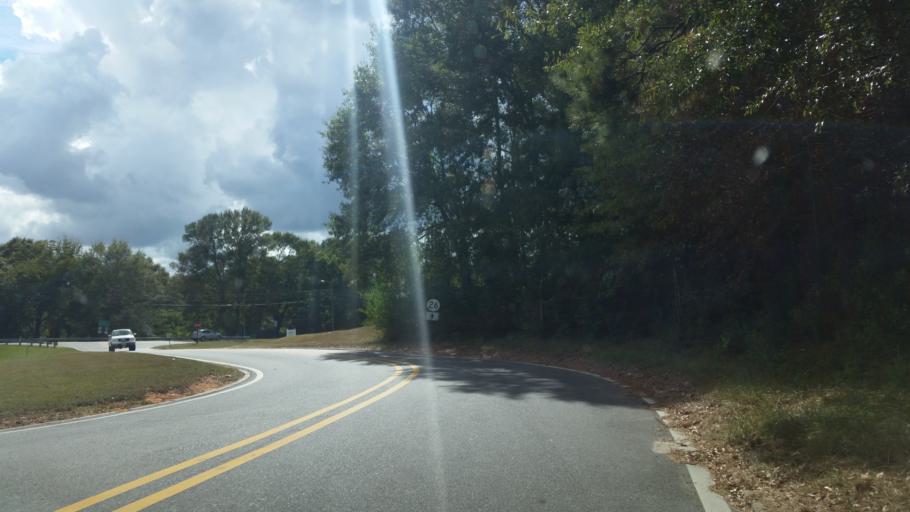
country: US
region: Mississippi
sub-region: Stone County
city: Wiggins
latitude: 30.8529
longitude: -89.1387
